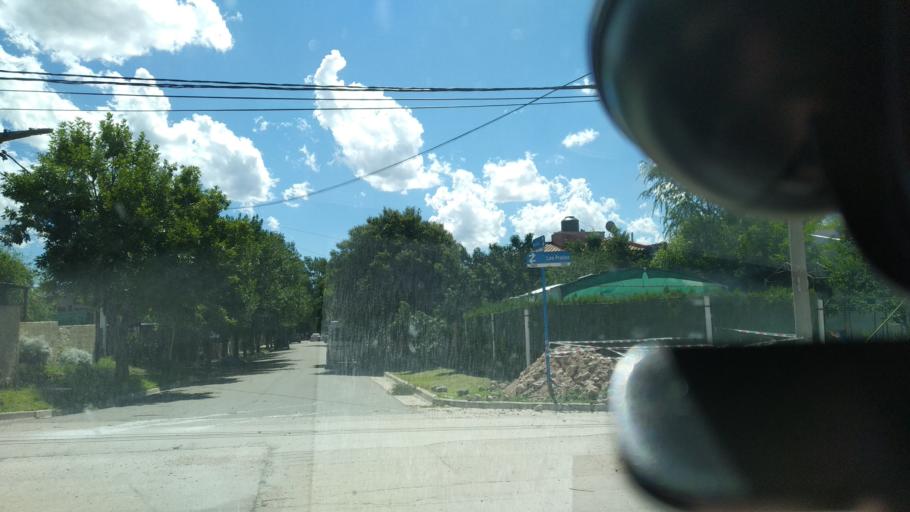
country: AR
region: Cordoba
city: Mina Clavero
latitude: -31.7241
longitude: -65.0108
